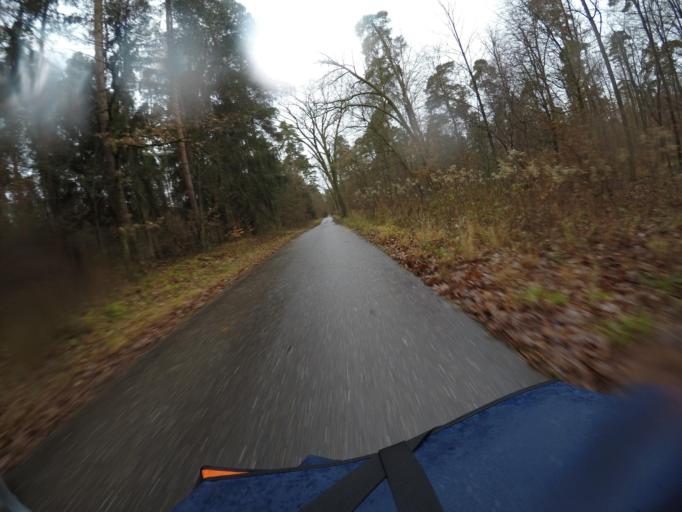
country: DE
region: Baden-Wuerttemberg
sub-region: Karlsruhe Region
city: Eggenstein-Leopoldshafen
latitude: 49.0803
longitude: 8.4544
